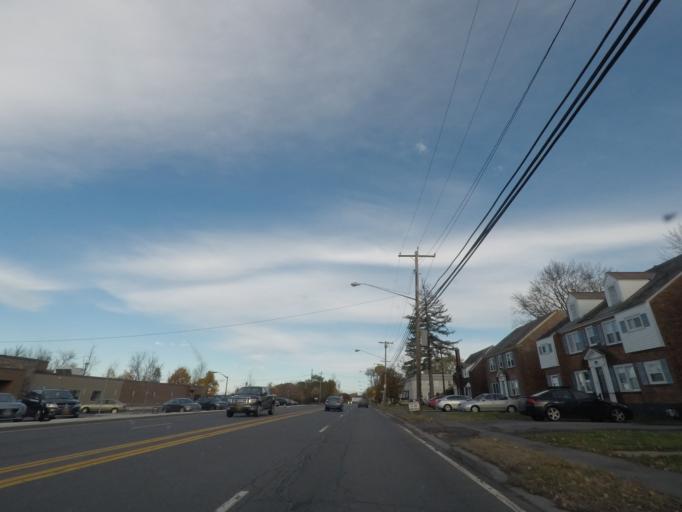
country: US
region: New York
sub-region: Albany County
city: Delmar
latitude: 42.6298
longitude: -73.8079
